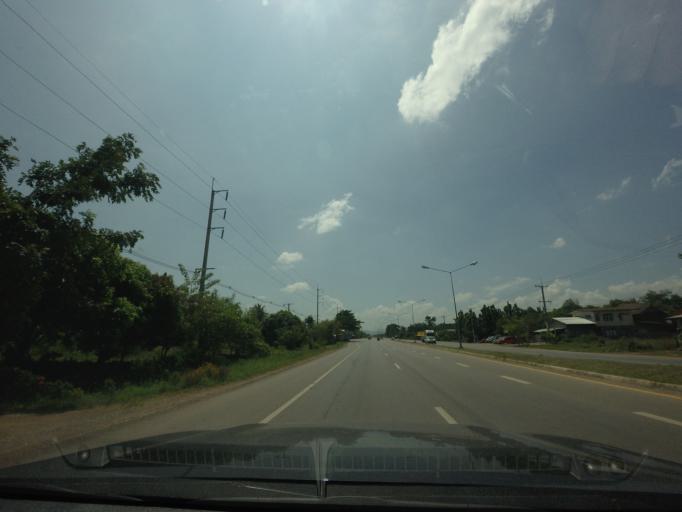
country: TH
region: Phetchabun
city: Lom Sak
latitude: 16.7219
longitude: 101.1843
